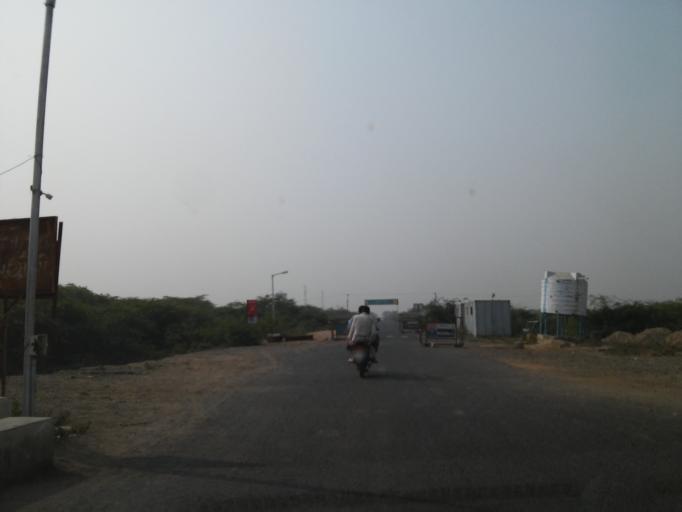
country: IN
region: Gujarat
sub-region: Kachchh
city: Bhuj
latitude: 23.6688
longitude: 69.7099
